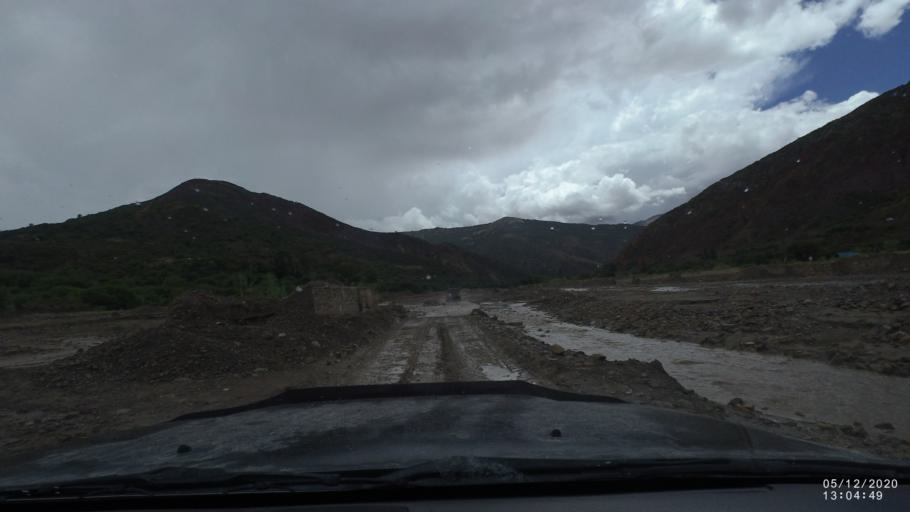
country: BO
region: Cochabamba
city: Sipe Sipe
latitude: -17.5528
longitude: -66.4414
